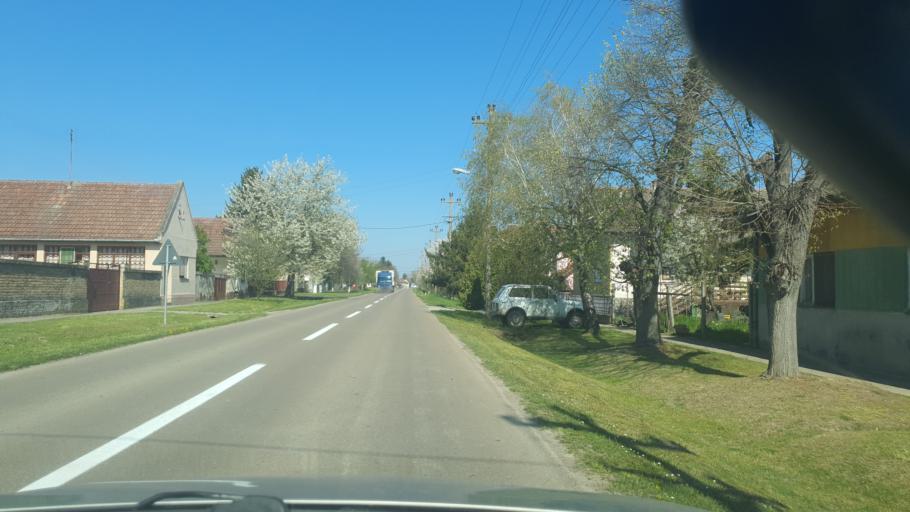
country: RS
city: Kolut
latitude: 45.8849
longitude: 18.9299
